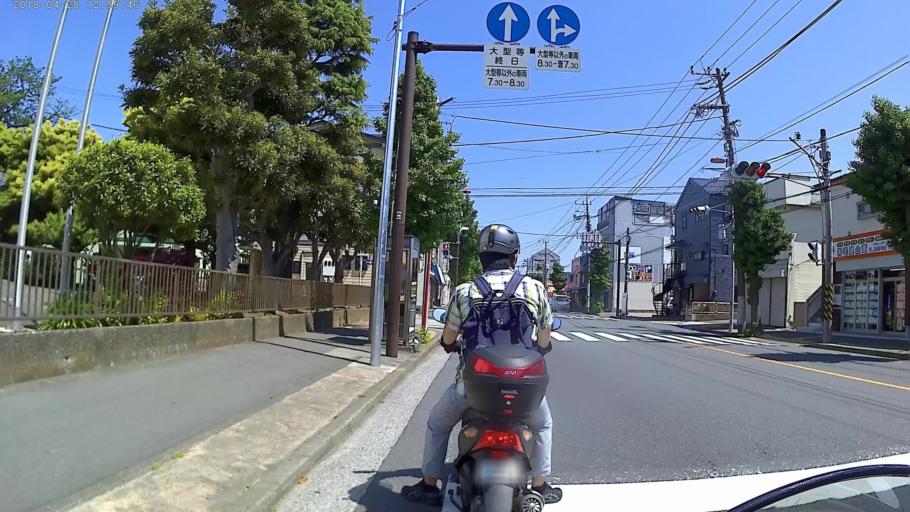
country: JP
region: Kanagawa
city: Yokosuka
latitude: 35.2534
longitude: 139.6743
